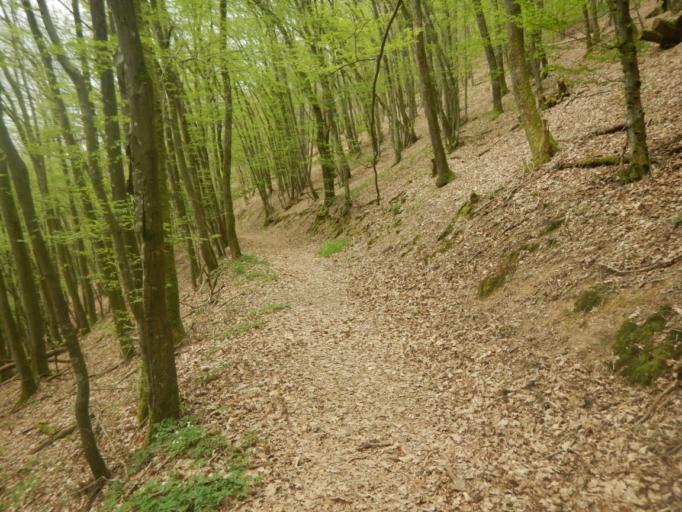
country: LU
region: Diekirch
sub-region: Canton de Wiltz
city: Esch-sur-Sure
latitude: 49.9140
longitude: 5.9378
